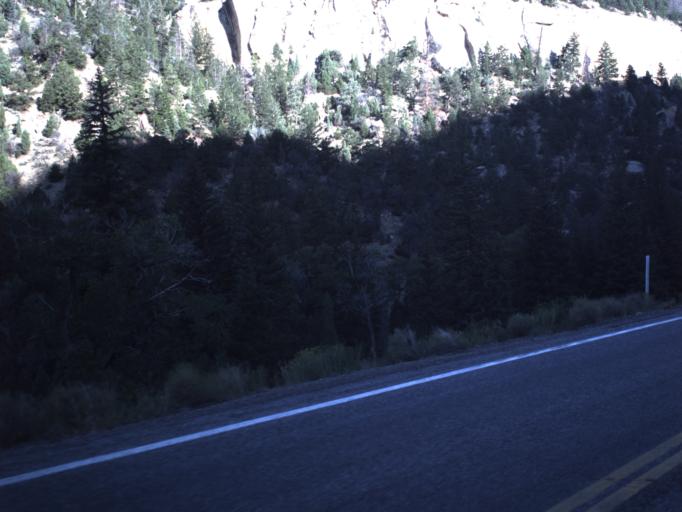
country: US
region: Utah
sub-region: Emery County
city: Huntington
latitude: 39.4266
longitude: -111.1295
